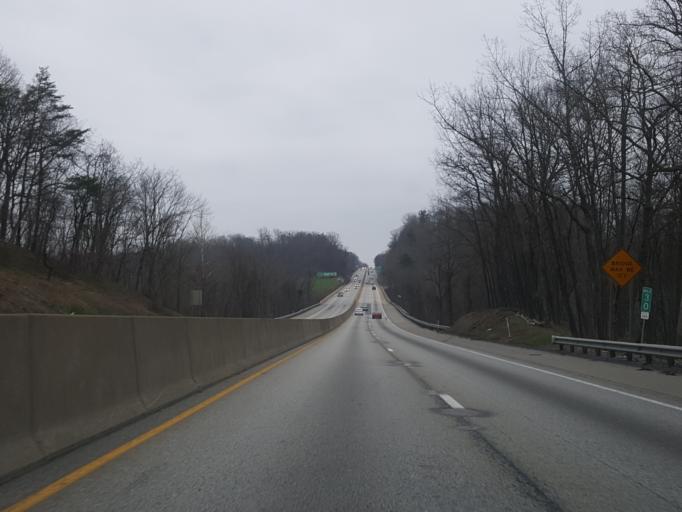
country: US
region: Pennsylvania
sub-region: York County
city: Valley Green
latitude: 40.1057
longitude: -76.7808
